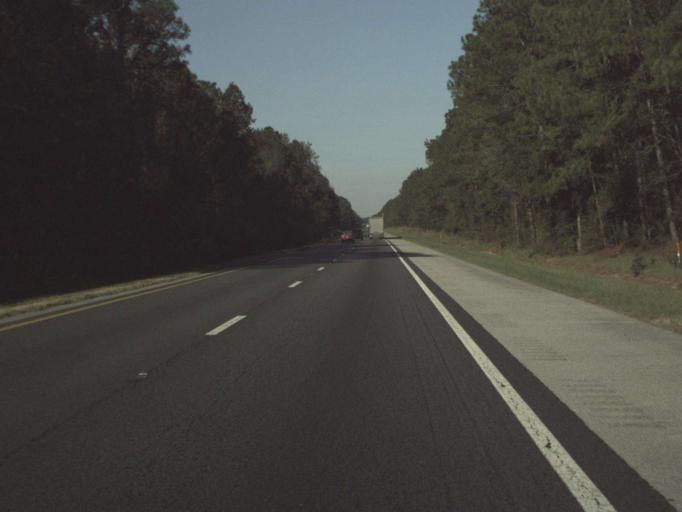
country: US
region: Florida
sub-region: Holmes County
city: Bonifay
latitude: 30.7613
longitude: -85.7647
